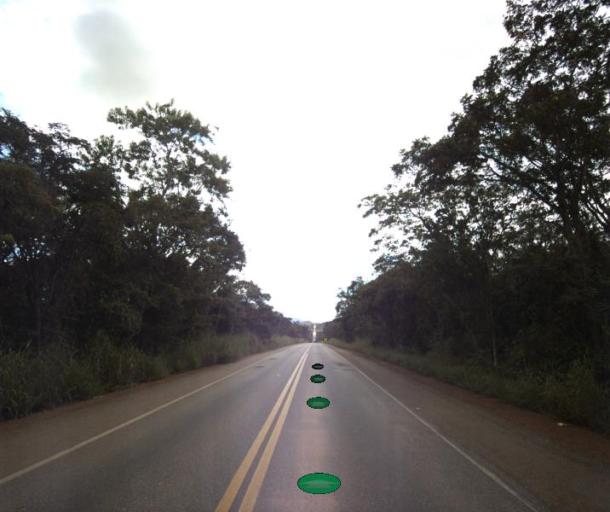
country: BR
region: Goias
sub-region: Jaragua
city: Jaragua
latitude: -15.9187
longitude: -49.2177
